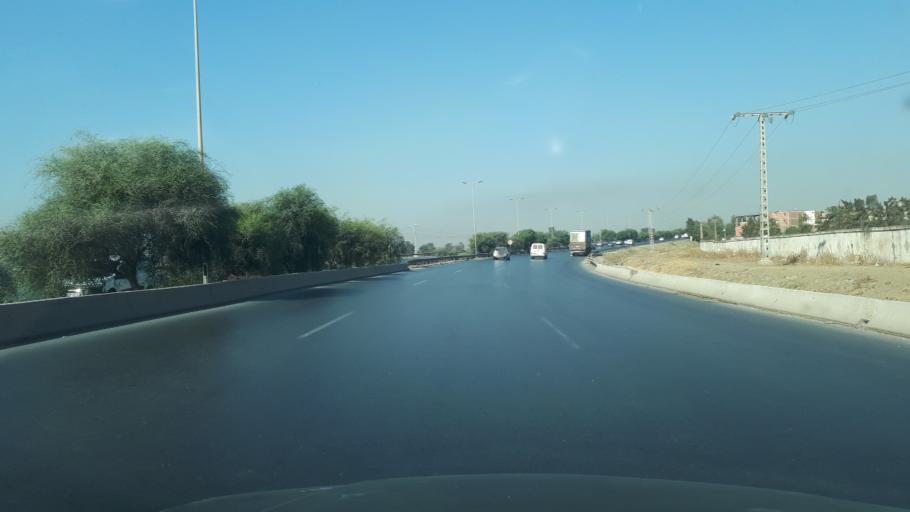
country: DZ
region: Tipaza
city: Baraki
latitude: 36.6822
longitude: 3.1077
